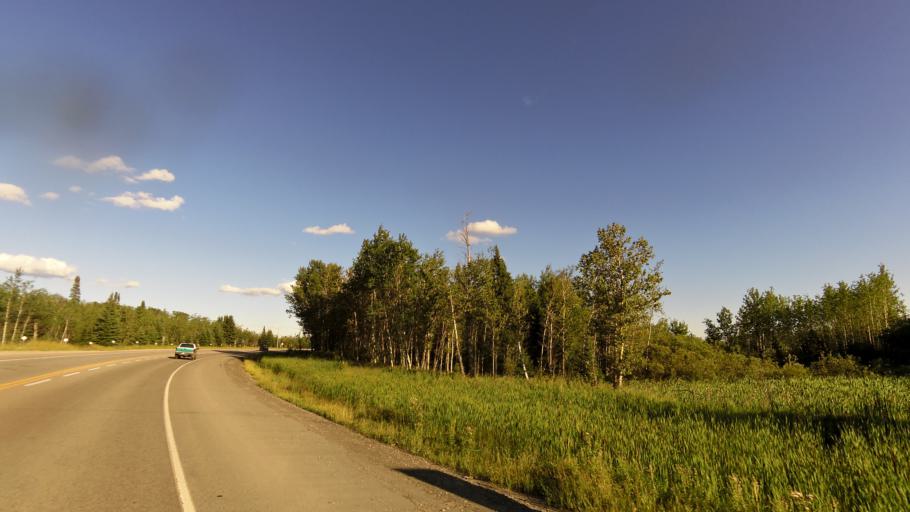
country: CA
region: Ontario
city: Dryden
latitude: 49.8151
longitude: -92.8519
